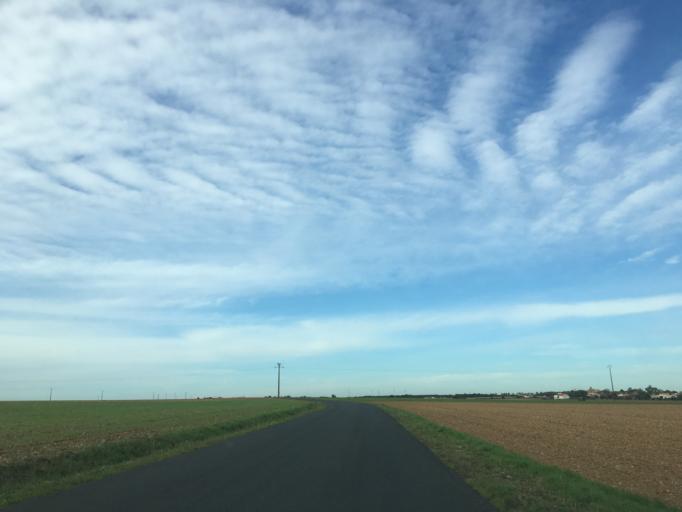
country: FR
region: Poitou-Charentes
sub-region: Departement des Deux-Sevres
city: Beauvoir-sur-Niort
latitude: 46.0704
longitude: -0.4855
